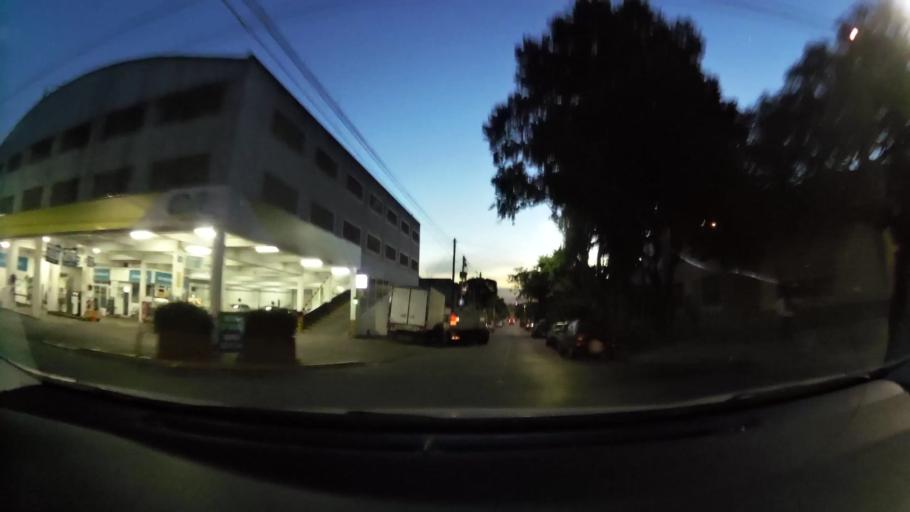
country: AR
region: Buenos Aires F.D.
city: Villa Lugano
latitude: -34.6850
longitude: -58.4790
